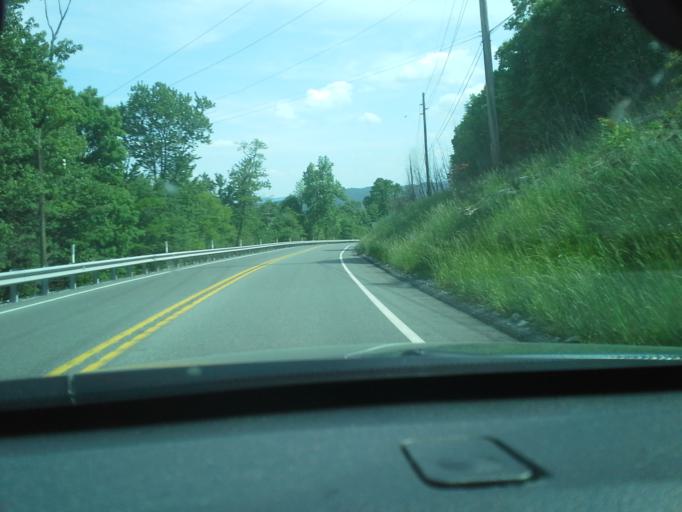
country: US
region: Pennsylvania
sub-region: Fulton County
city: McConnellsburg
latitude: 39.8836
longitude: -77.9657
